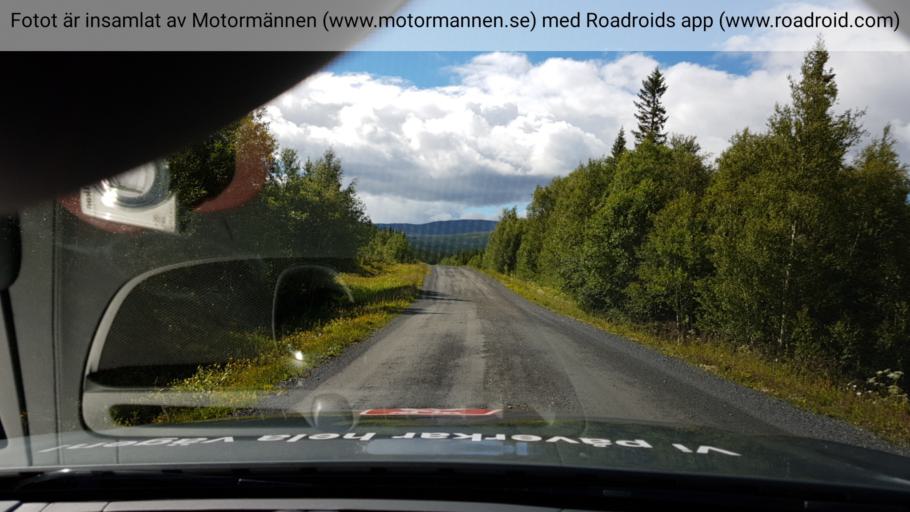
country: SE
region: Jaemtland
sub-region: Krokoms Kommun
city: Valla
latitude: 63.0968
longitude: 13.8925
